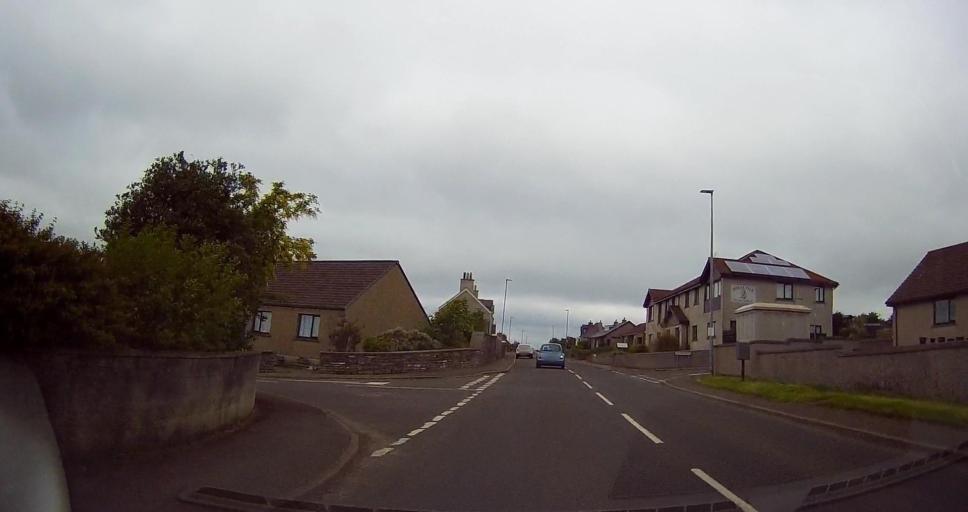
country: GB
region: Scotland
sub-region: Orkney Islands
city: Kirkwall
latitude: 58.9726
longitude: -2.9528
